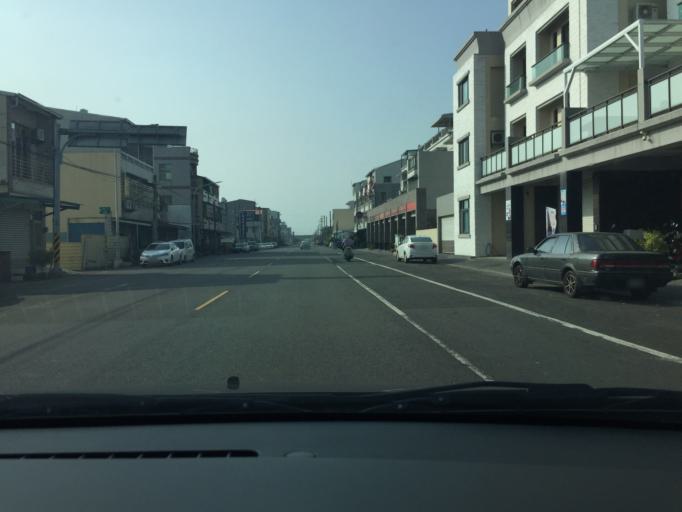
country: TW
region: Taiwan
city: Xinying
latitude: 23.1947
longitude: 120.3063
